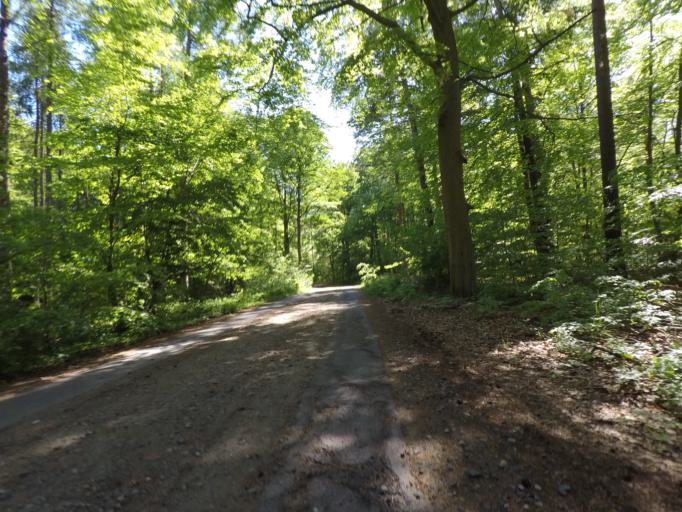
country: DE
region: Brandenburg
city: Eberswalde
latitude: 52.8205
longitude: 13.7787
